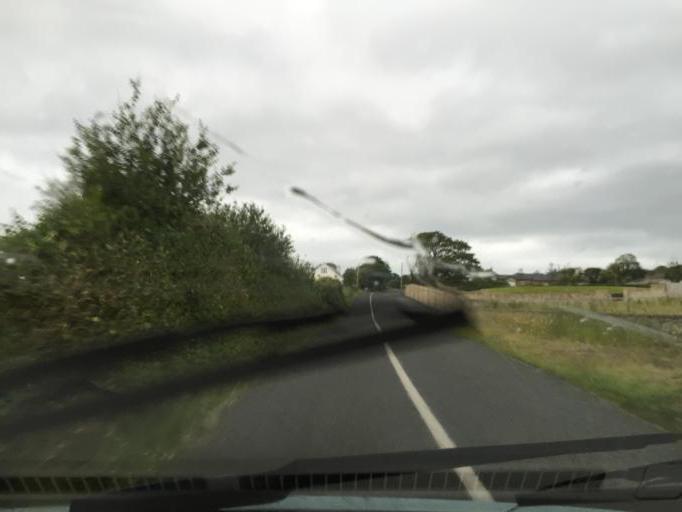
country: IE
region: Connaught
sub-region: Sligo
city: Strandhill
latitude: 54.2589
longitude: -8.5972
